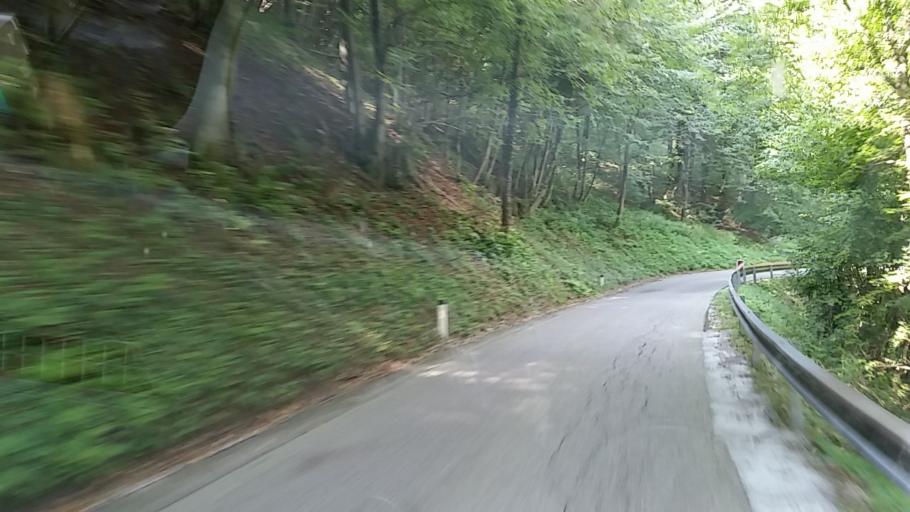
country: SI
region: Tolmin
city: Tolmin
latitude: 46.1318
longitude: 13.7796
